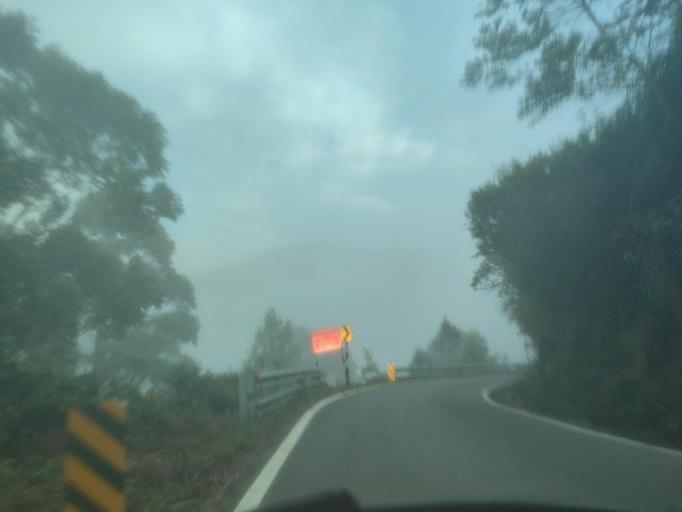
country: IN
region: Tamil Nadu
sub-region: Dindigul
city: Kodaikanal
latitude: 10.3178
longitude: 77.5654
